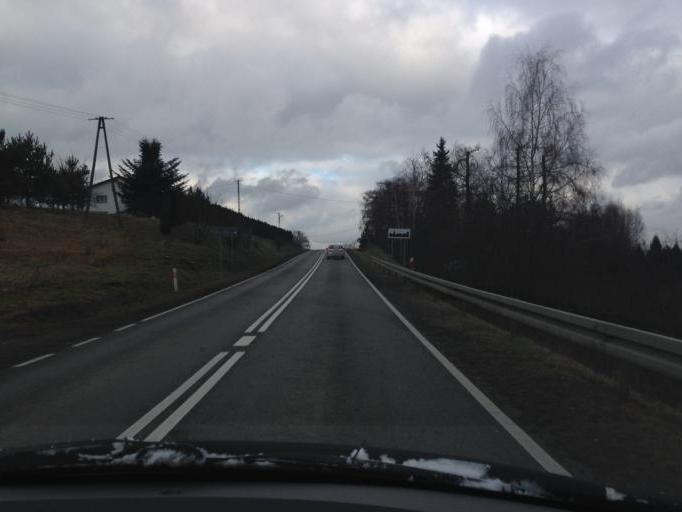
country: PL
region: Lesser Poland Voivodeship
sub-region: Powiat wielicki
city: Gdow
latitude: 49.9051
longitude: 20.1598
